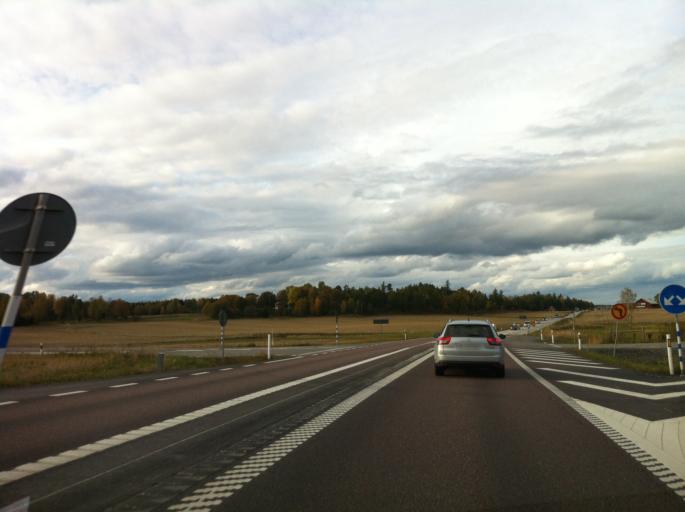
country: SE
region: OErebro
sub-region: Askersunds Kommun
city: Askersund
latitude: 58.8549
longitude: 14.9075
